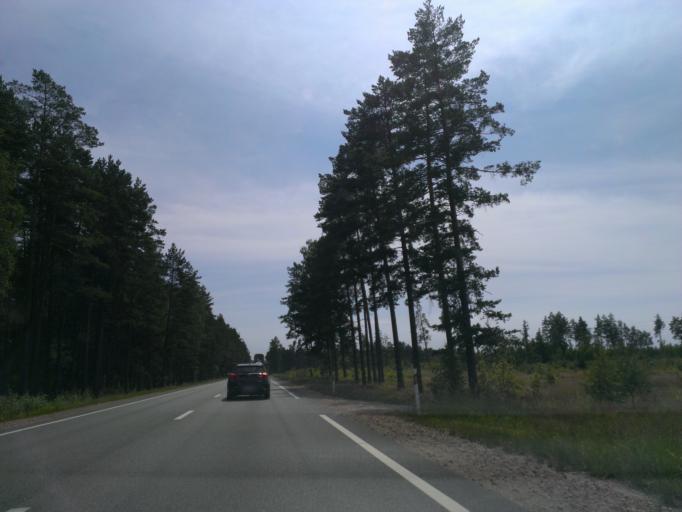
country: LV
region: Salaspils
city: Salaspils
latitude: 56.9363
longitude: 24.3857
